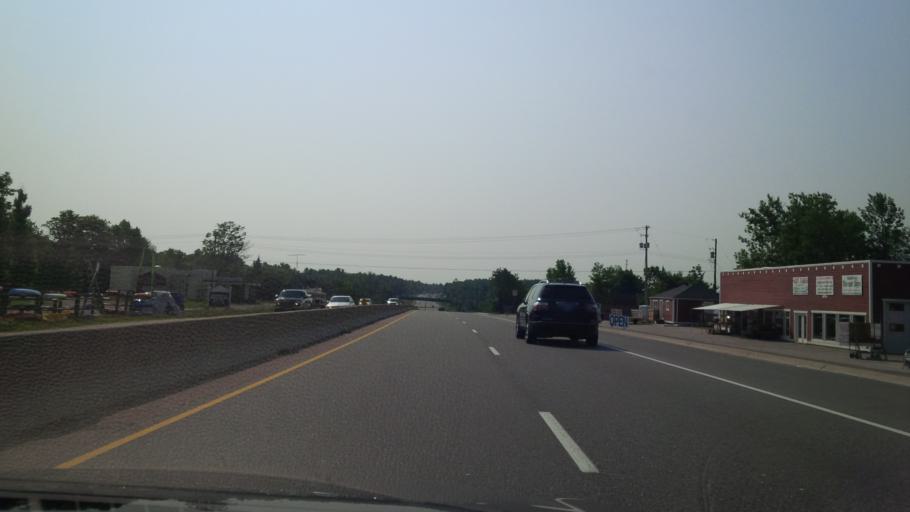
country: CA
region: Ontario
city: Gravenhurst
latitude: 44.8828
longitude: -79.3440
